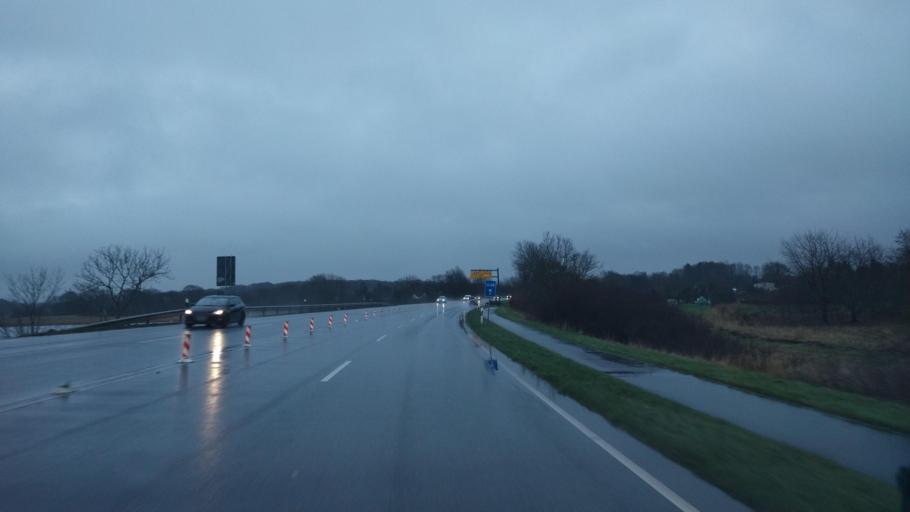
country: DE
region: Schleswig-Holstein
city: Busdorf
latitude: 54.5049
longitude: 9.5500
